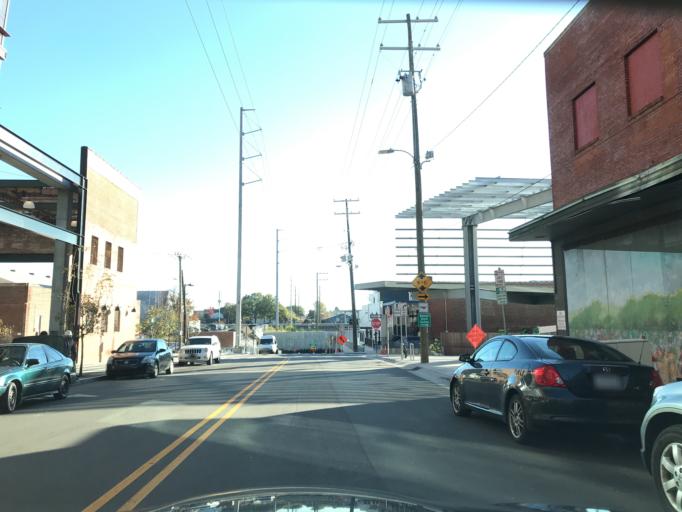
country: US
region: North Carolina
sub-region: Wake County
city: Raleigh
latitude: 35.7777
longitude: -78.6461
